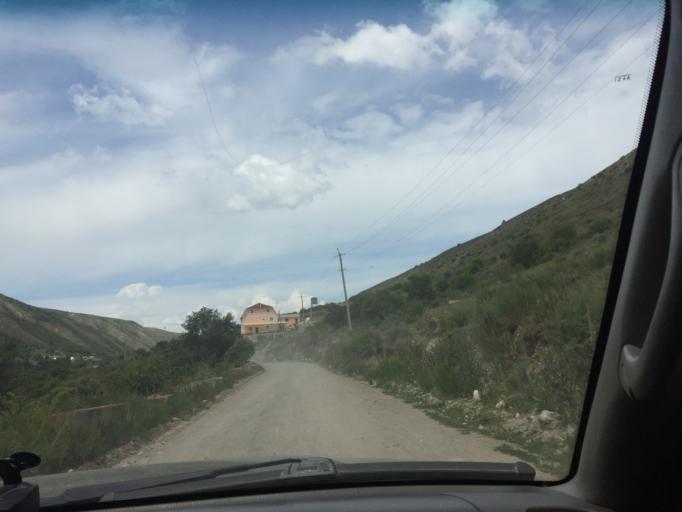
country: KG
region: Ysyk-Koel
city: Karakol
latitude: 42.4272
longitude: 78.4327
